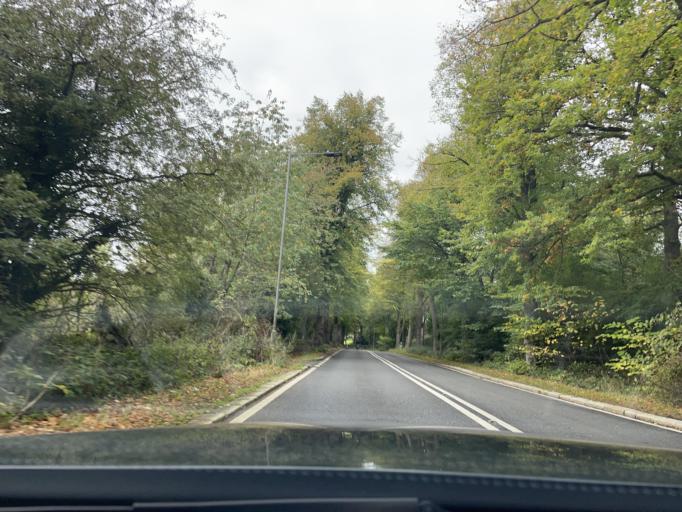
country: GB
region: England
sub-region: Sheffield
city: Oughtibridge
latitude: 53.3824
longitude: -1.5548
